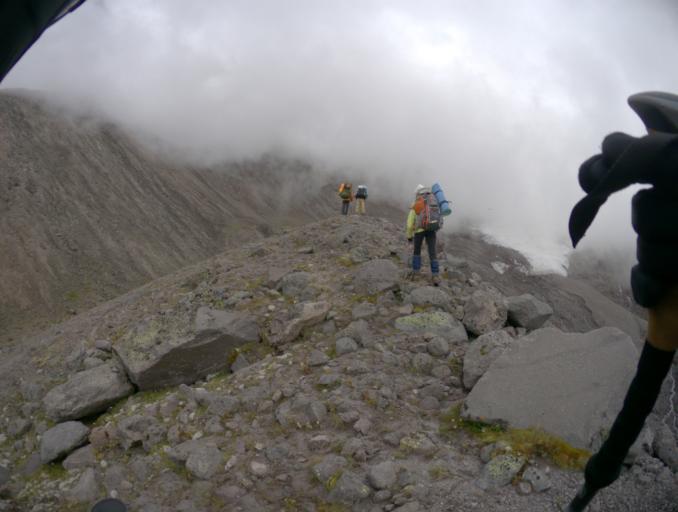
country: RU
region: Kabardino-Balkariya
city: Terskol
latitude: 43.3819
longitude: 42.3869
